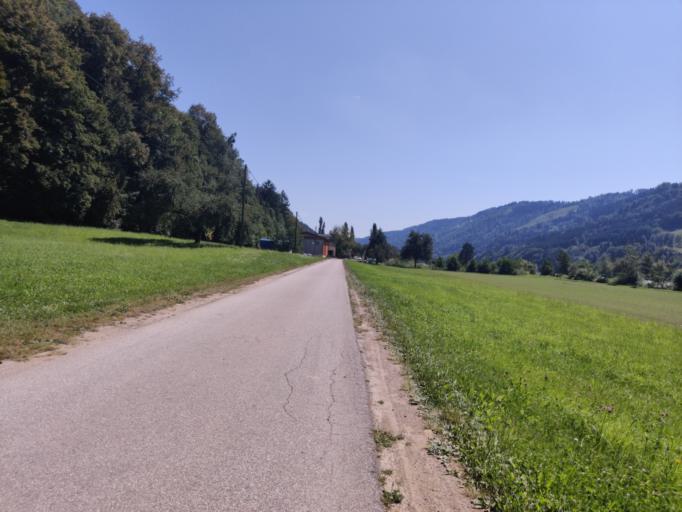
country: AT
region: Upper Austria
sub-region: Politischer Bezirk Rohrbach
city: Pfarrkirchen im Muehlkreis
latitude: 48.4526
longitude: 13.8251
